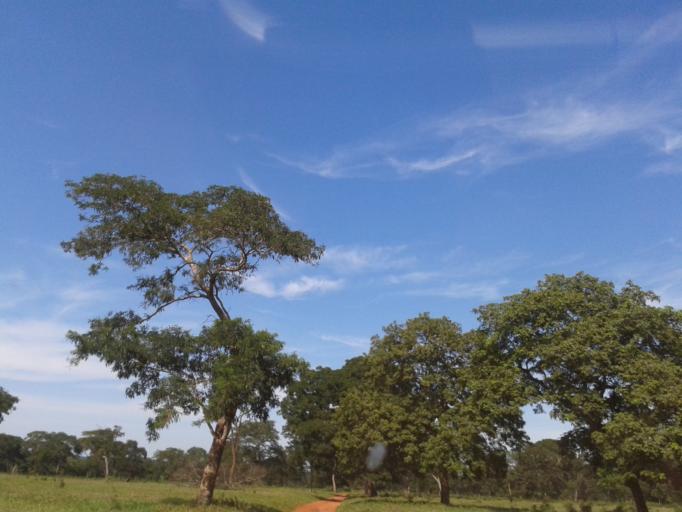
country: BR
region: Minas Gerais
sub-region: Santa Vitoria
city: Santa Vitoria
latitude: -19.1633
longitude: -50.5114
